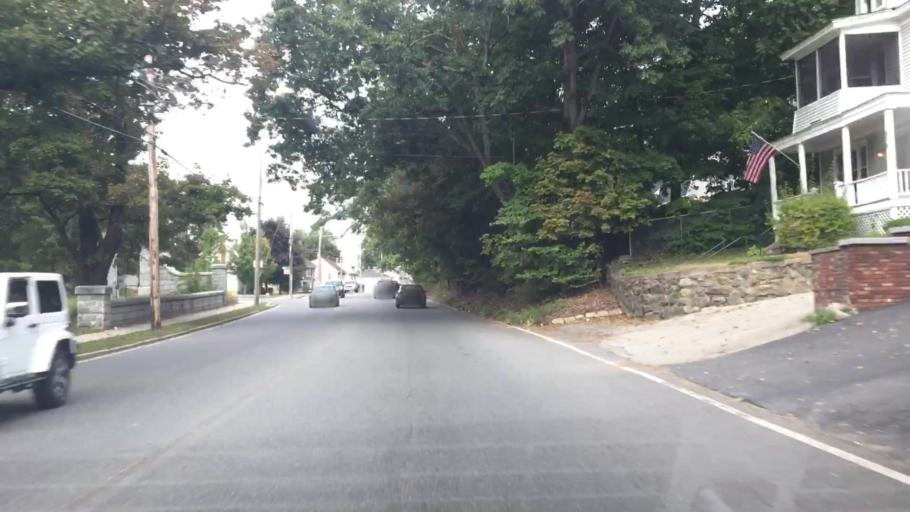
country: US
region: Massachusetts
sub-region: Middlesex County
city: Lowell
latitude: 42.6331
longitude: -71.2894
